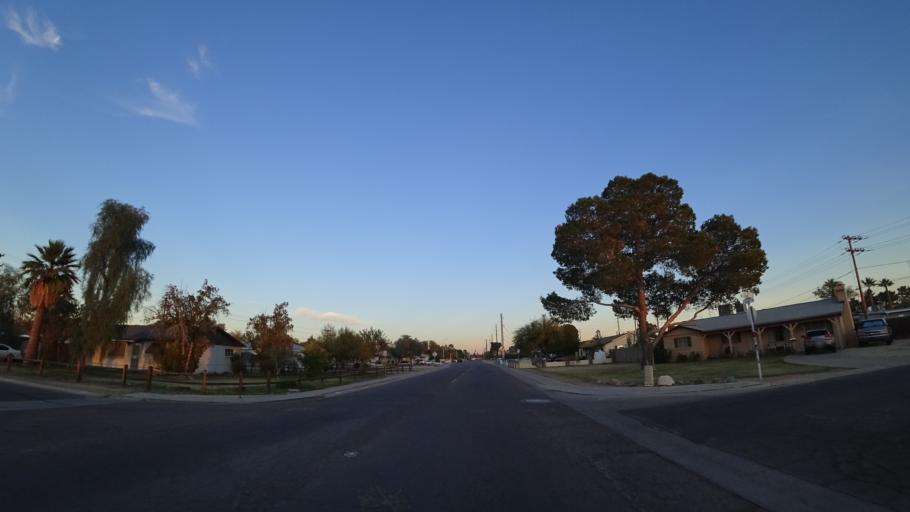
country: US
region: Arizona
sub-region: Maricopa County
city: Phoenix
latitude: 33.4731
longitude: -112.0087
